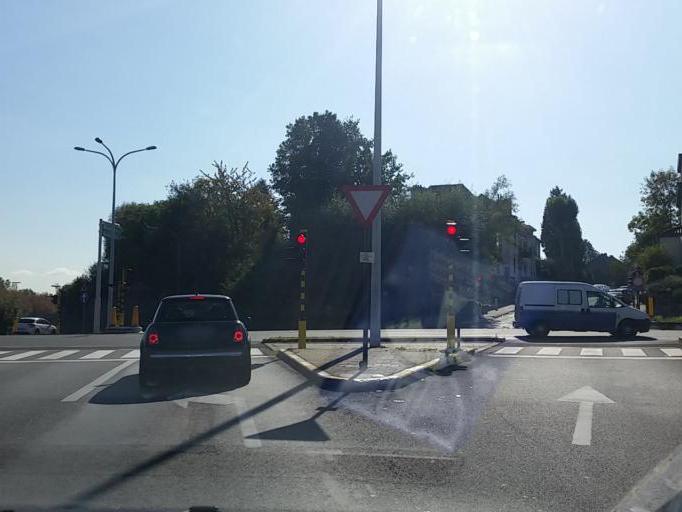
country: BE
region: Flanders
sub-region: Provincie Vlaams-Brabant
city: Dilbeek
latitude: 50.8456
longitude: 4.2796
